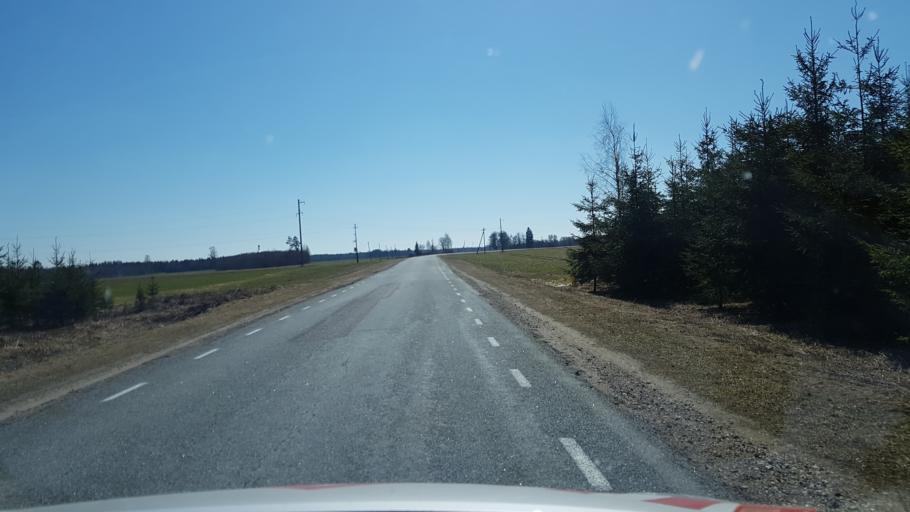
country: EE
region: Laeaene-Virumaa
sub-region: Rakke vald
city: Rakke
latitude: 59.0256
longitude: 26.3517
